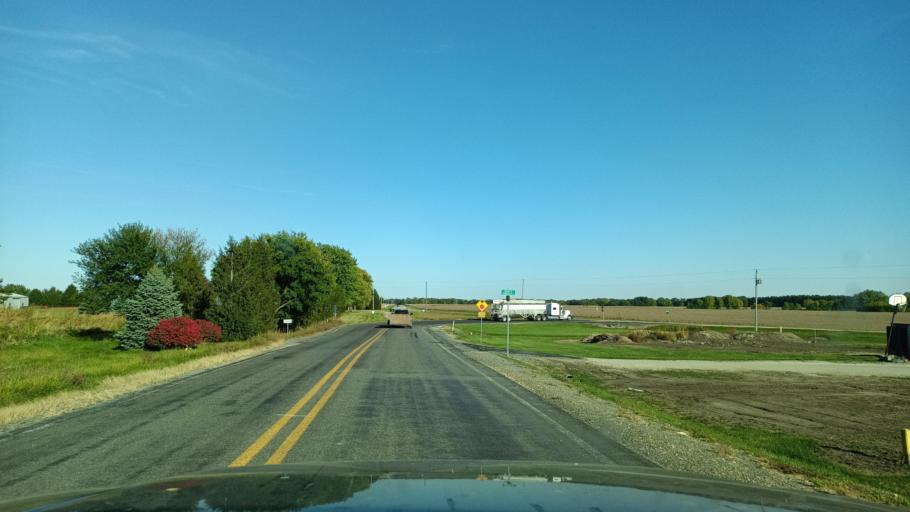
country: US
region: Illinois
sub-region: De Witt County
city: Farmer City
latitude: 40.2238
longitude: -88.7173
